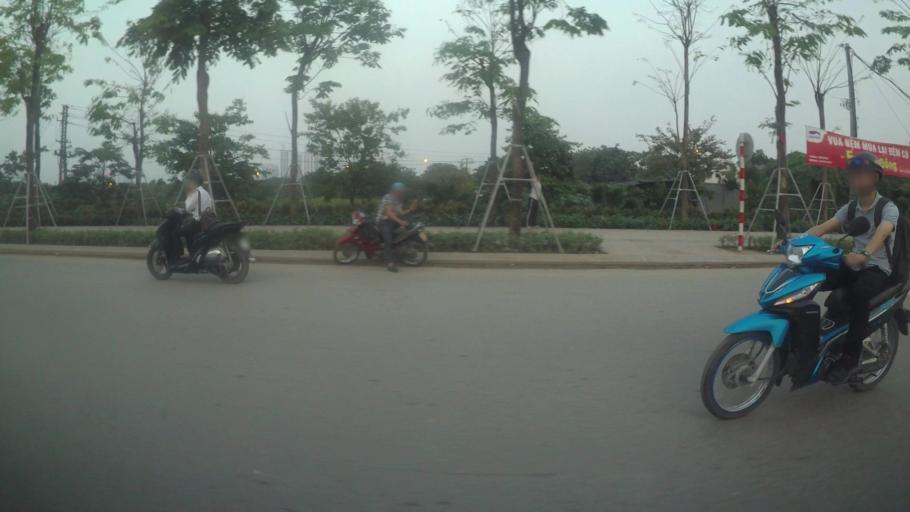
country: VN
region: Ha Noi
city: Tay Ho
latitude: 21.0618
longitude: 105.7841
